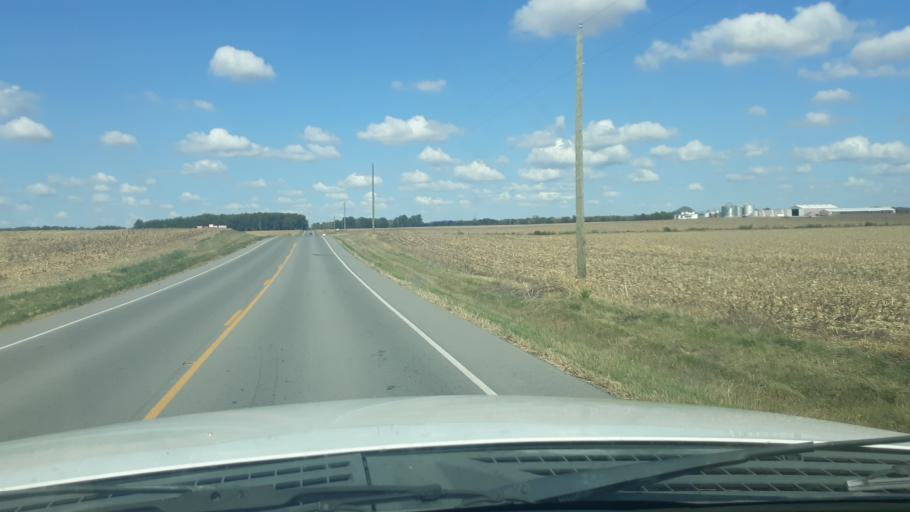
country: US
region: Illinois
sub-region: Saline County
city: Eldorado
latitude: 37.7991
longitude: -88.4848
